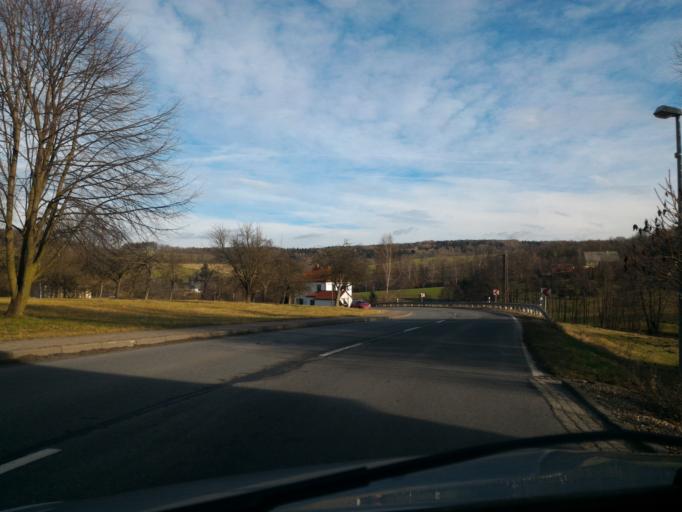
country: DE
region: Saxony
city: Steinigtwolmsdorf
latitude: 51.0728
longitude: 14.3404
